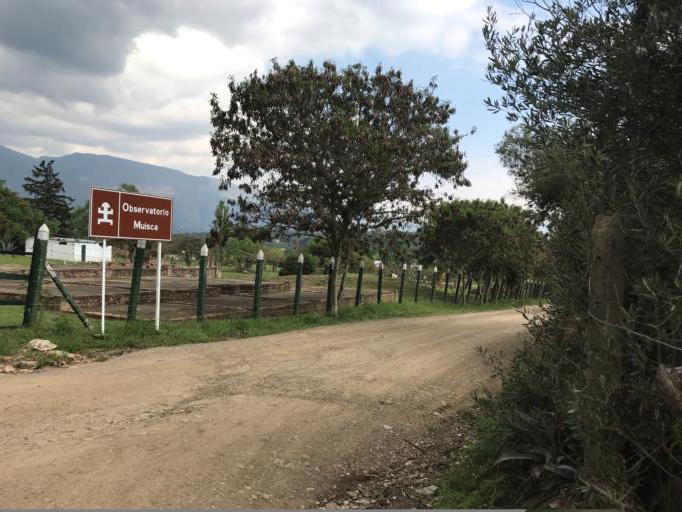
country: CO
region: Boyaca
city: Villa de Leiva
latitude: 5.6480
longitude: -73.5598
